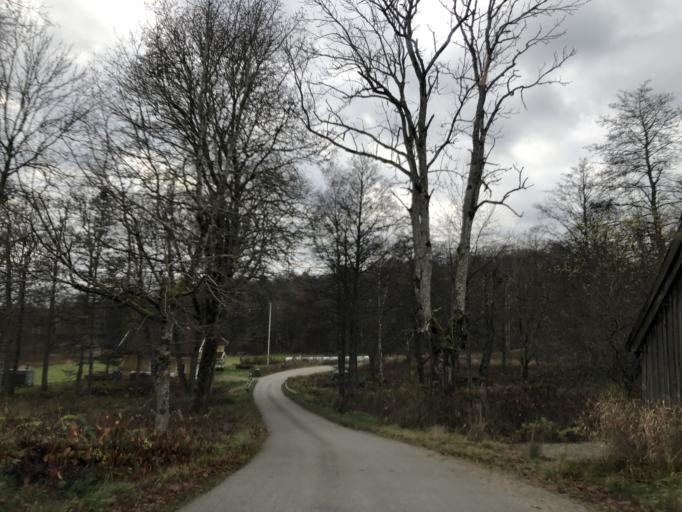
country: SE
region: Vaestra Goetaland
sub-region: Ulricehamns Kommun
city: Ulricehamn
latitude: 57.7309
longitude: 13.3697
